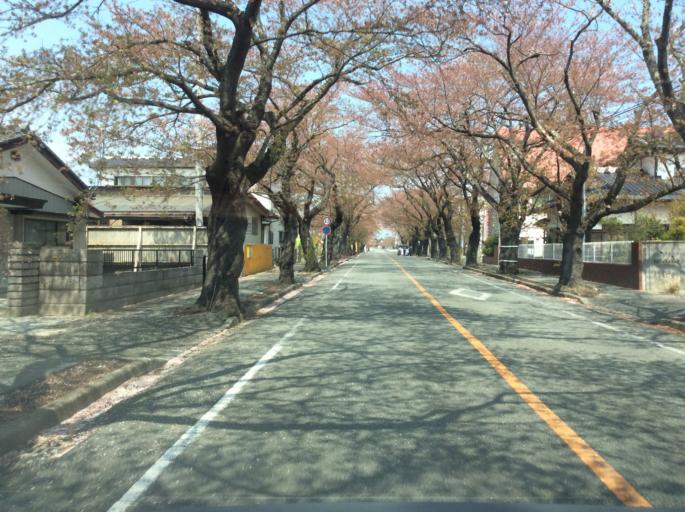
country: JP
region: Fukushima
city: Namie
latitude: 37.3600
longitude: 140.9959
